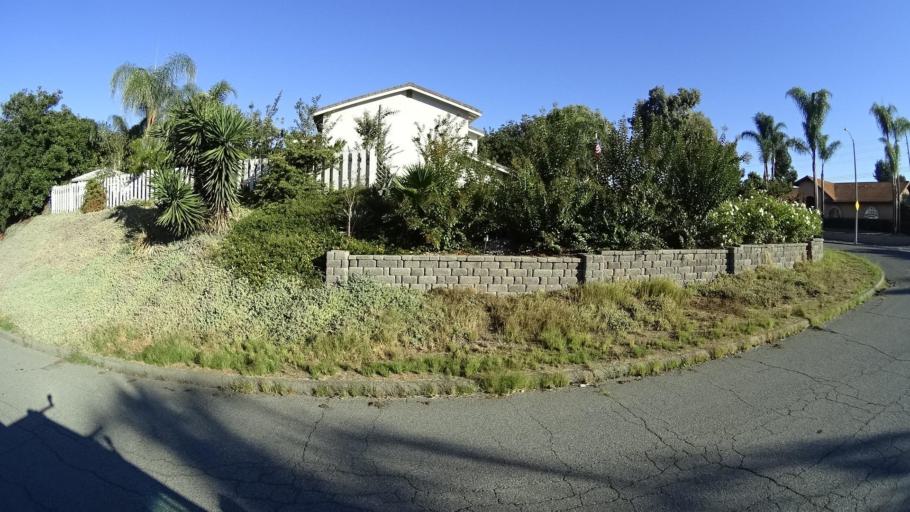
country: US
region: California
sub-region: San Diego County
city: Bonita
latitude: 32.6728
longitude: -117.0303
